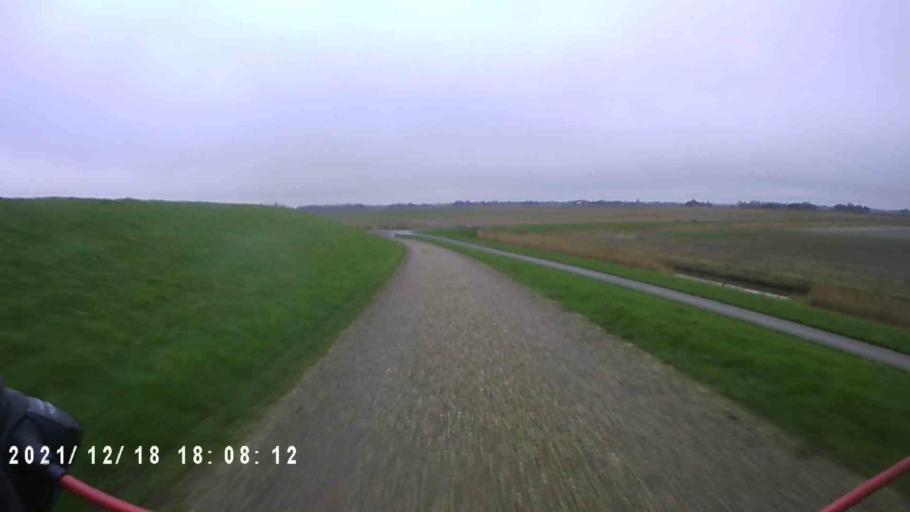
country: NL
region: Friesland
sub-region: Gemeente Dongeradeel
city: Holwerd
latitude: 53.3854
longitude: 5.9219
